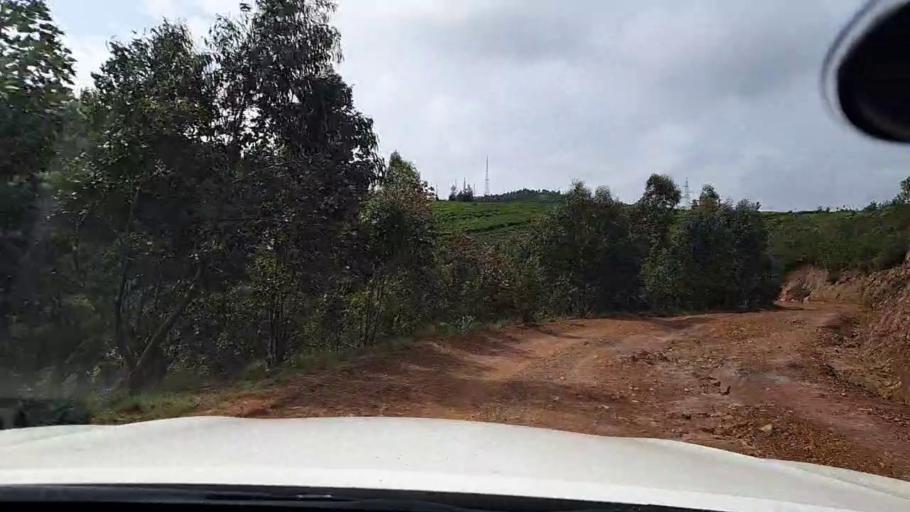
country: RW
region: Western Province
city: Kibuye
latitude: -2.1377
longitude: 29.3766
